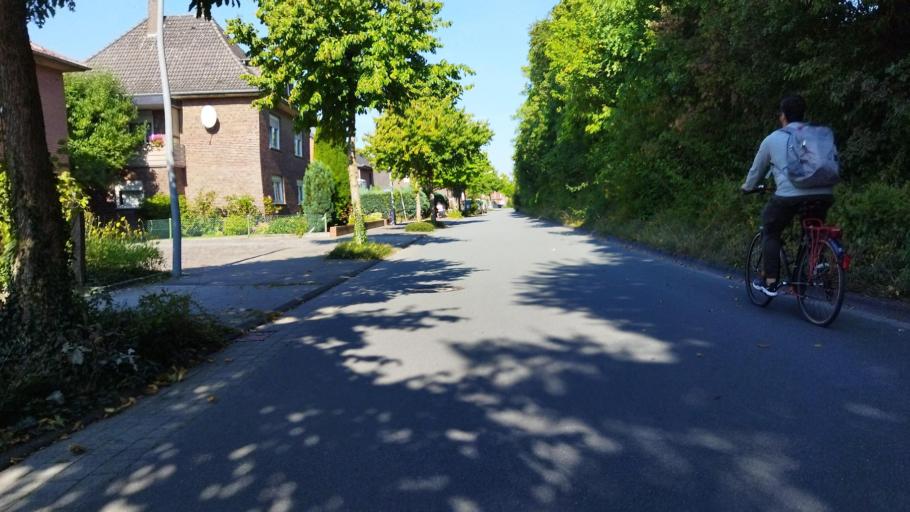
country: DE
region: North Rhine-Westphalia
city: Lengerich
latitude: 52.1784
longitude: 7.8736
